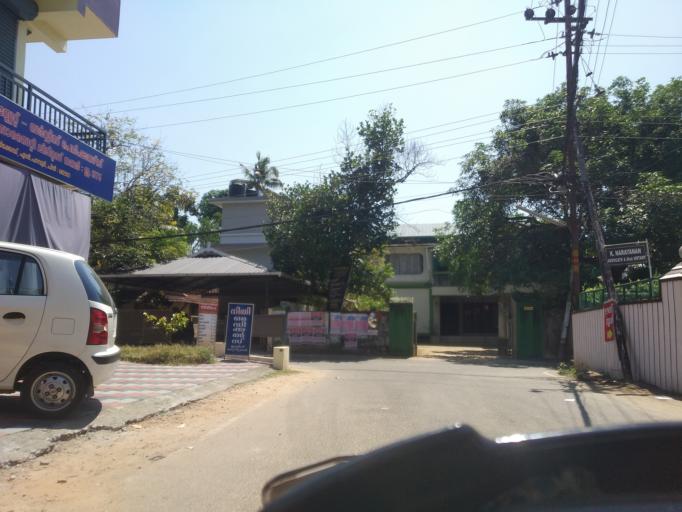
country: IN
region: Kerala
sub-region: Thrissur District
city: Kodungallur
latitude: 10.1469
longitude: 76.2312
